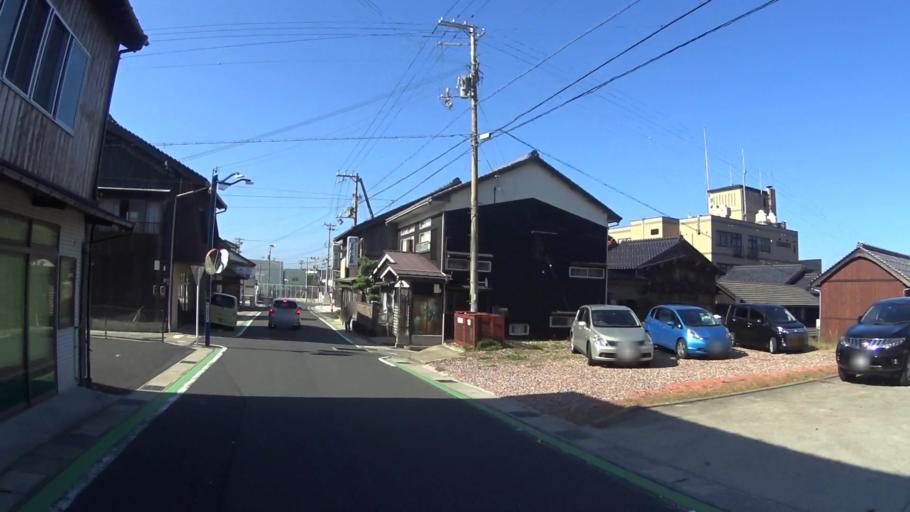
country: JP
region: Kyoto
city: Miyazu
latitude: 35.7367
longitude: 135.0893
